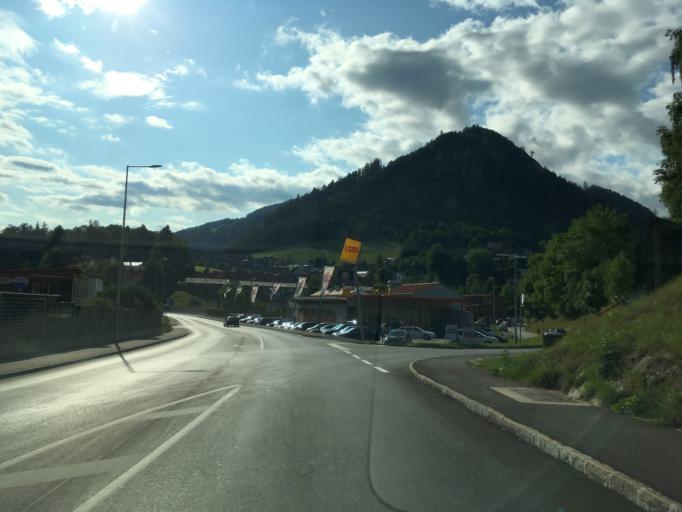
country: AT
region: Styria
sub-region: Politischer Bezirk Murau
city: Murau
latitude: 47.1139
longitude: 14.1753
